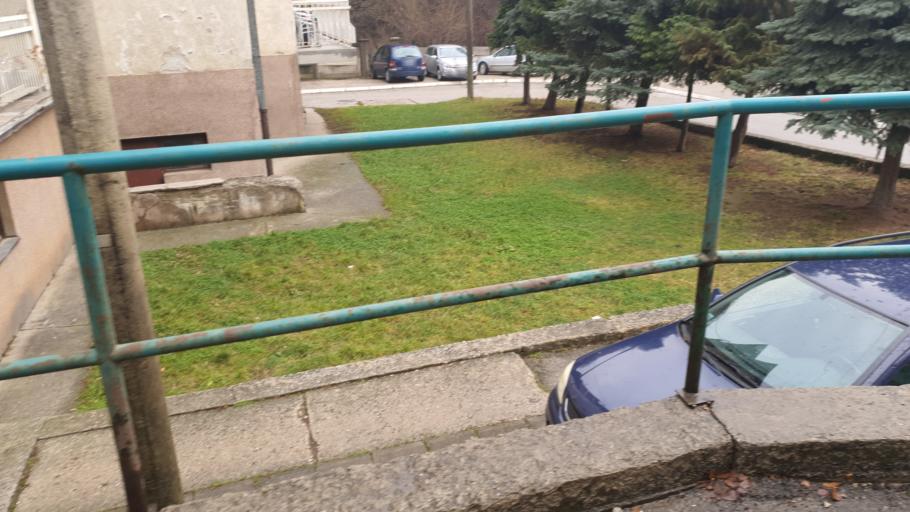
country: RS
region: Central Serbia
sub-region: Zlatiborski Okrug
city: Uzice
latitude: 43.8650
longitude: 19.8245
